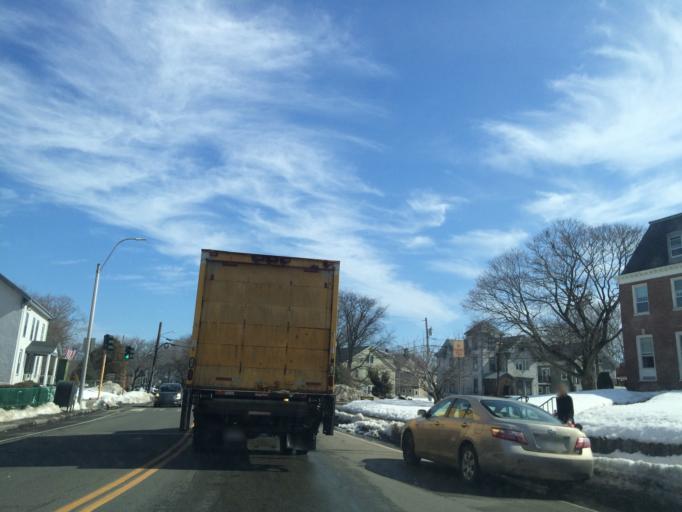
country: US
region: Massachusetts
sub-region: Middlesex County
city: Arlington
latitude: 42.4162
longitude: -71.1490
